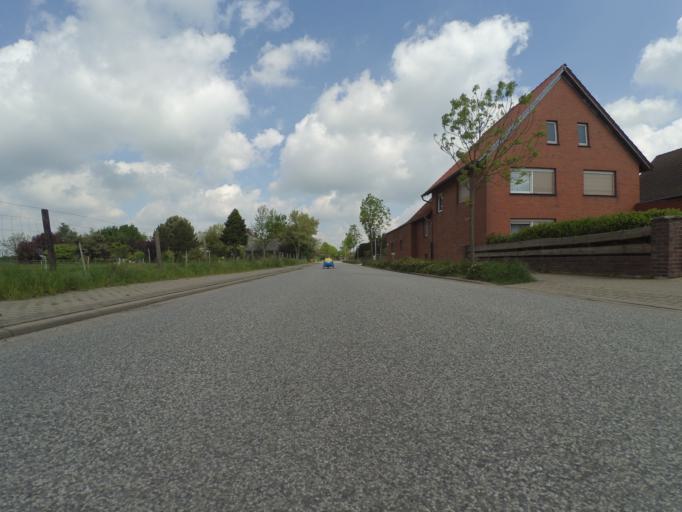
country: DE
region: Lower Saxony
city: Edemissen
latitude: 52.3415
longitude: 10.3154
